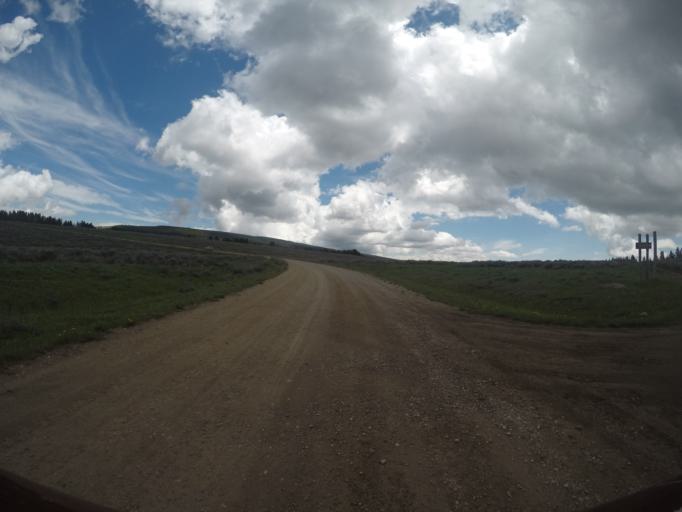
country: US
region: Wyoming
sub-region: Big Horn County
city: Lovell
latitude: 45.1717
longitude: -108.4539
